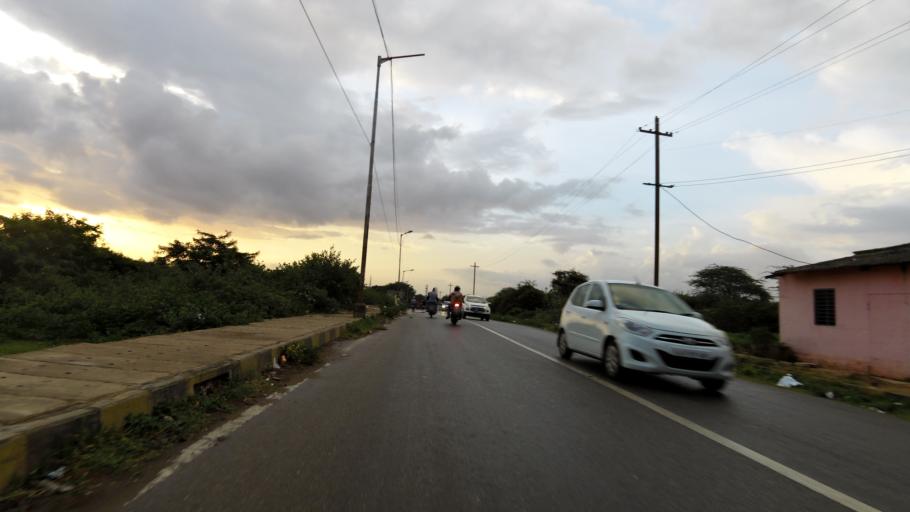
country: IN
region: Karnataka
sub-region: Bangalore Urban
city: Bangalore
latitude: 12.9967
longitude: 77.6421
